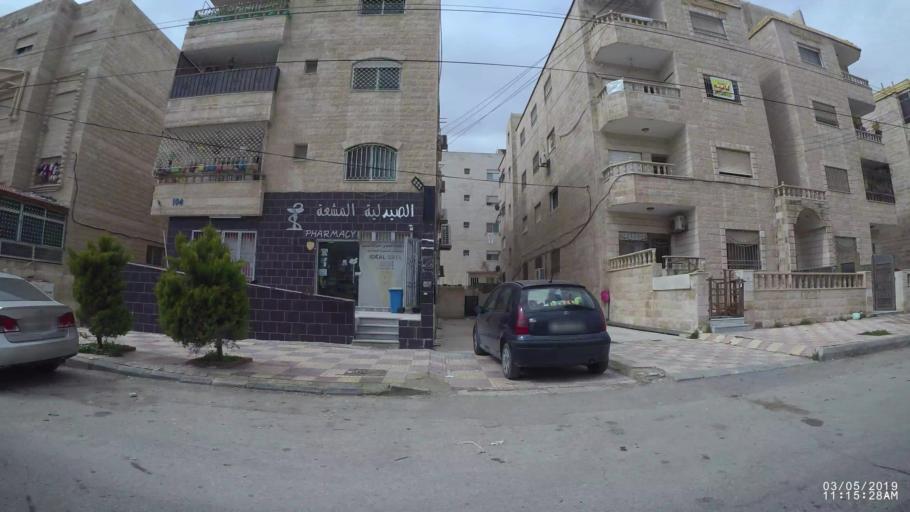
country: JO
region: Amman
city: Amman
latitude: 31.9887
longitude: 35.9283
